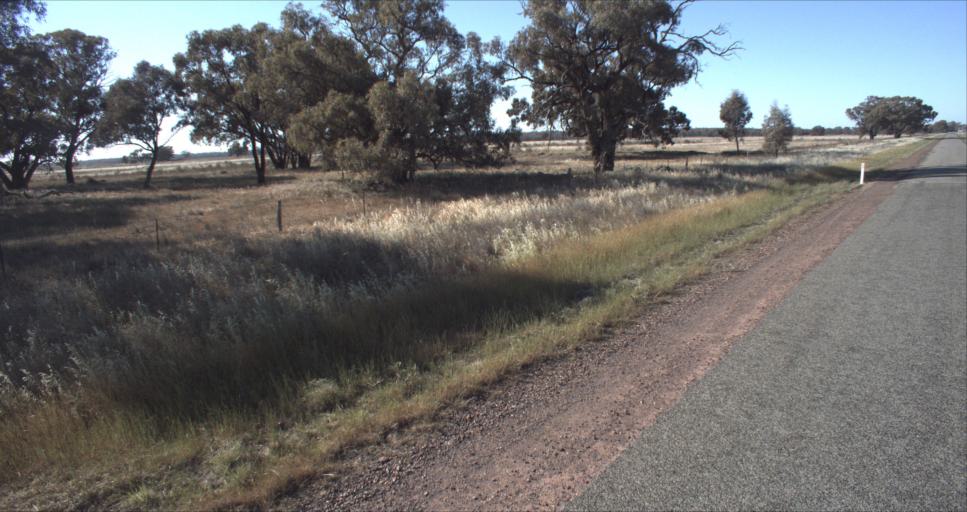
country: AU
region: New South Wales
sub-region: Leeton
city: Leeton
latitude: -34.5897
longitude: 146.2599
